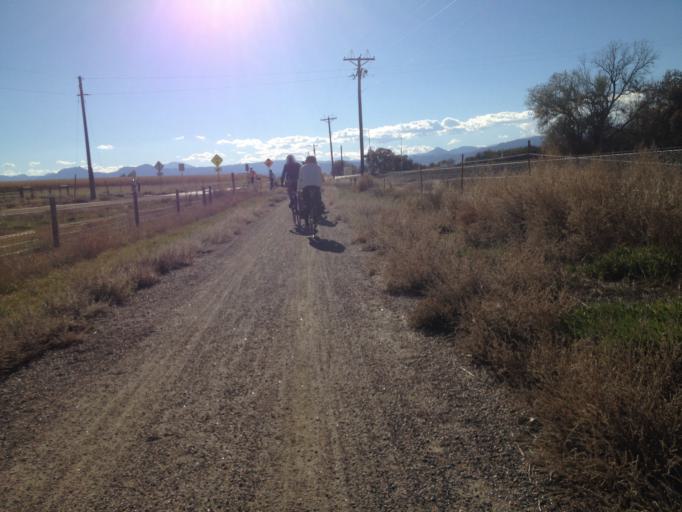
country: US
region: Colorado
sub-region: Boulder County
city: Niwot
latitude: 40.1227
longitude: -105.1479
